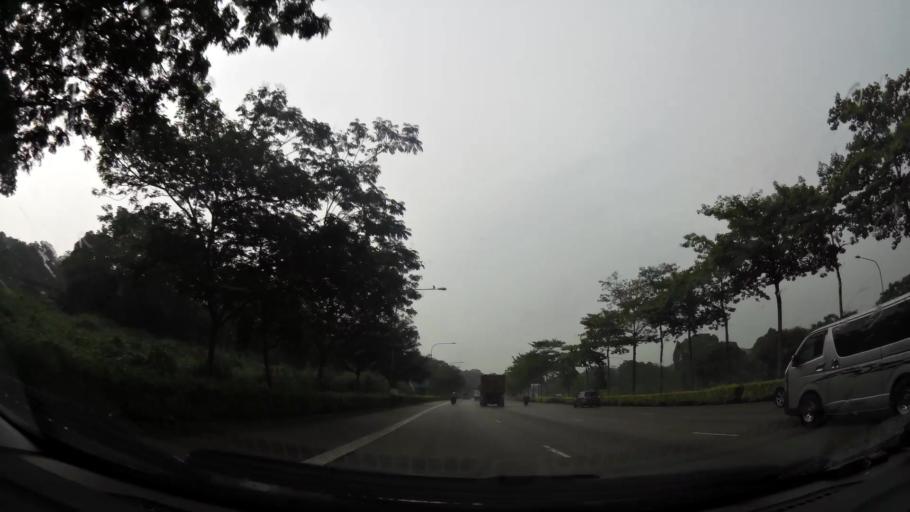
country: MY
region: Johor
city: Kampung Pasir Gudang Baru
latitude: 1.3928
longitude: 103.8269
